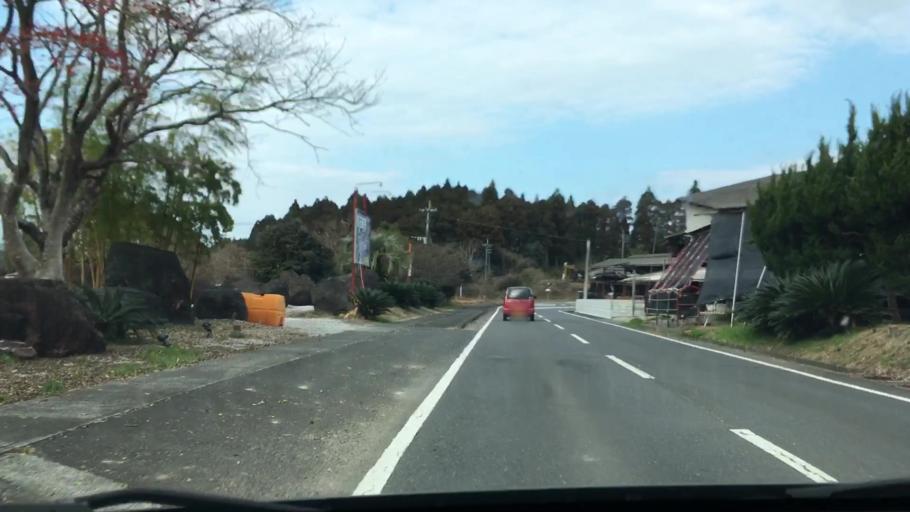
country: JP
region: Miyazaki
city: Kushima
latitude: 31.5030
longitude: 131.2388
